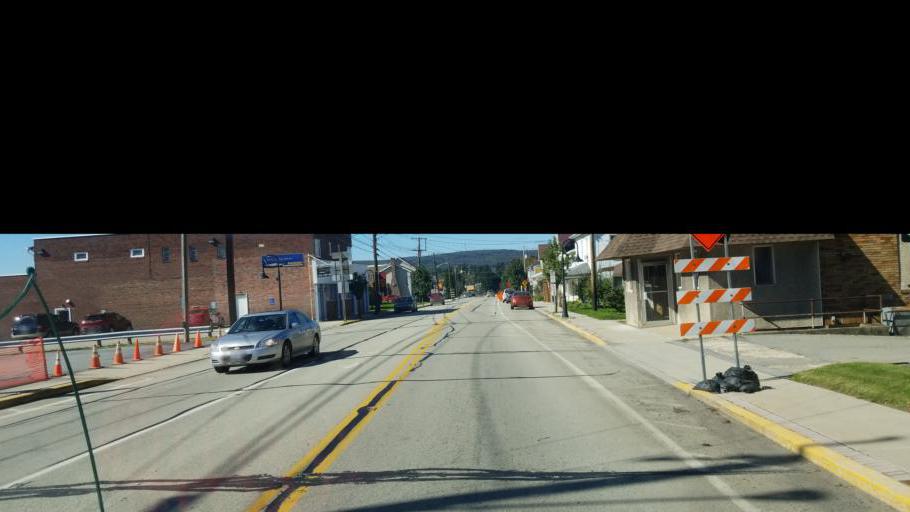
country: US
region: Pennsylvania
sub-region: Somerset County
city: Boswell
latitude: 40.1599
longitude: -79.0664
